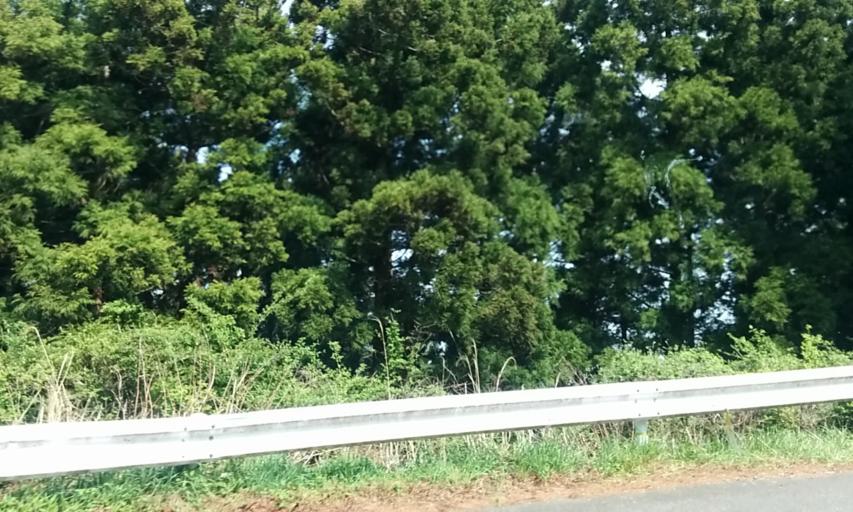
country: JP
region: Ehime
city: Niihama
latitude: 33.8794
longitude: 133.3093
